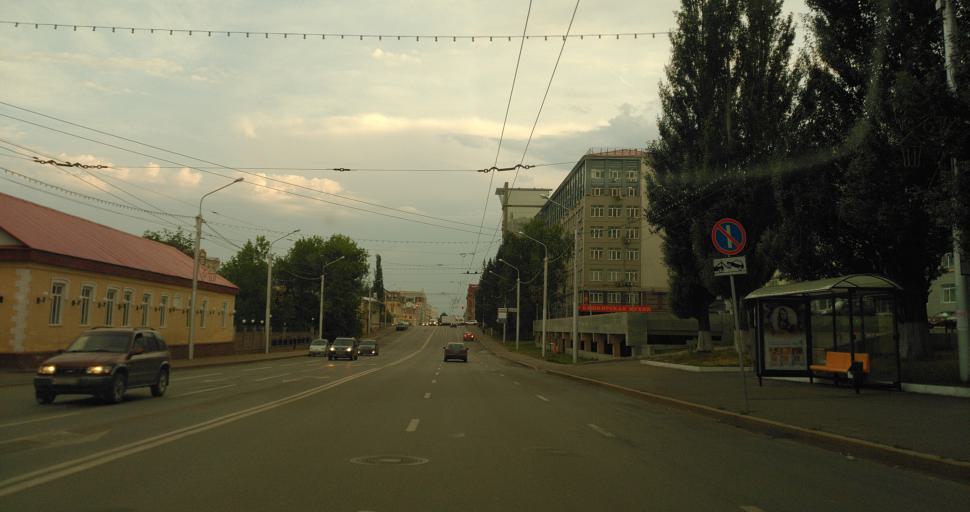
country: RU
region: Bashkortostan
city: Ufa
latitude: 54.7231
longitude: 55.9514
